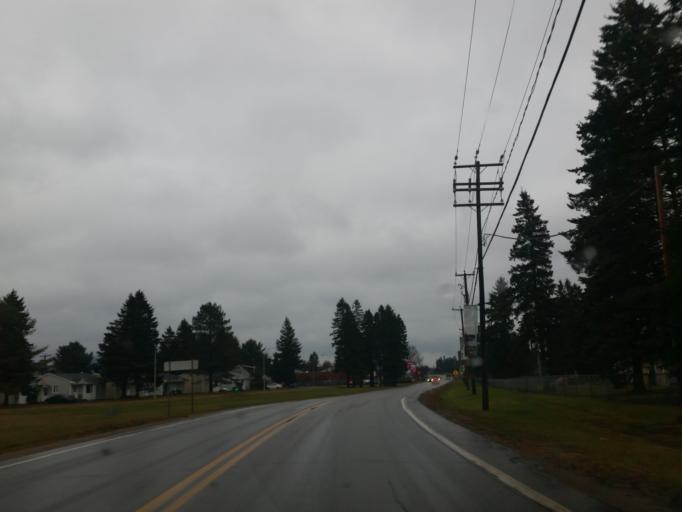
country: CA
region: Quebec
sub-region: Capitale-Nationale
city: Shannon
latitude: 46.8874
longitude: -71.5140
